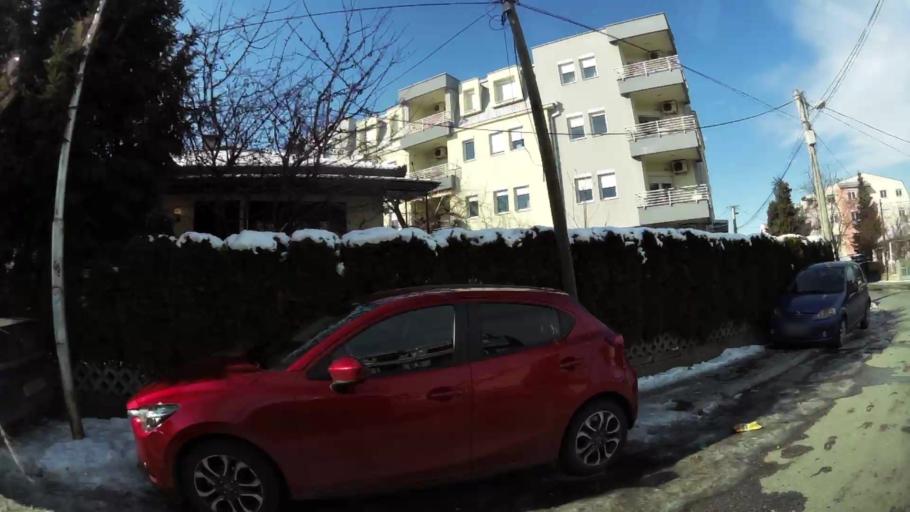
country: MK
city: Krushopek
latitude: 42.0044
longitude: 21.3686
